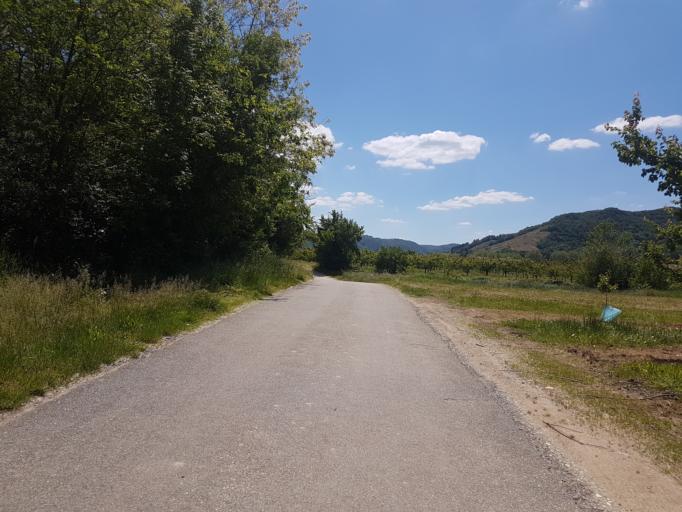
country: FR
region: Rhone-Alpes
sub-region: Departement de l'Ardeche
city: Saint-Jean-de-Muzols
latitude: 45.1026
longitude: 4.8215
